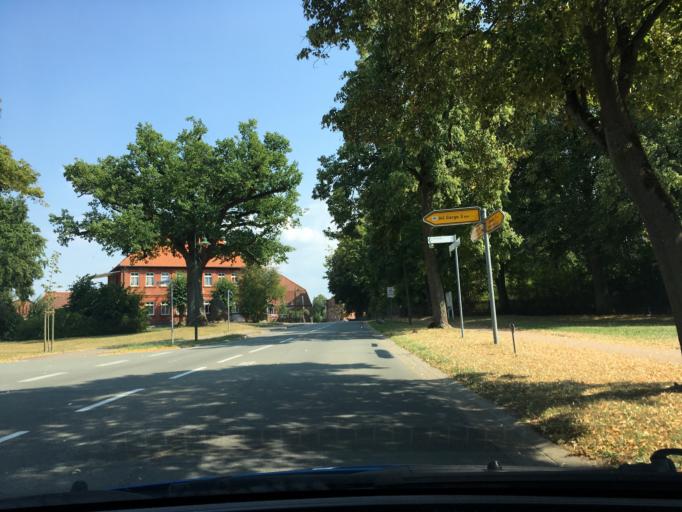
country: DE
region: Lower Saxony
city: Tosterglope
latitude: 53.2441
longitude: 10.7840
